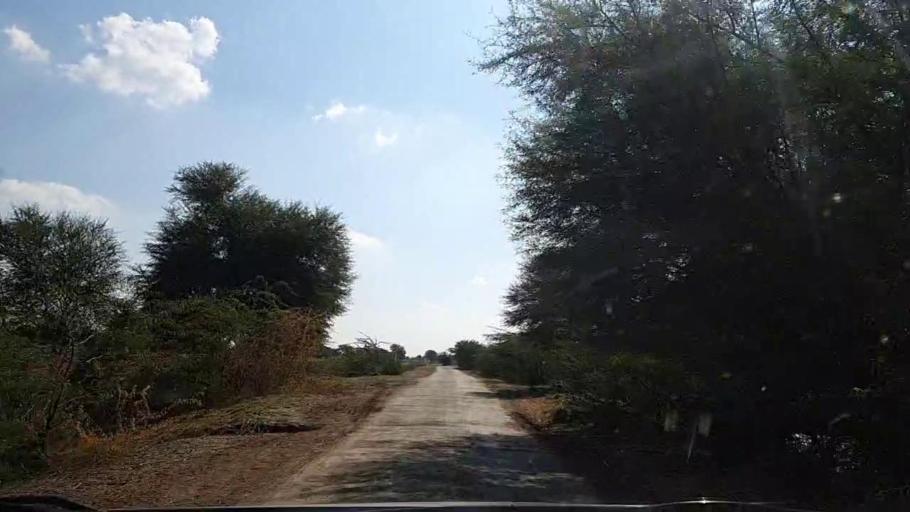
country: PK
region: Sindh
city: Pithoro
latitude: 25.6519
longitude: 69.4486
